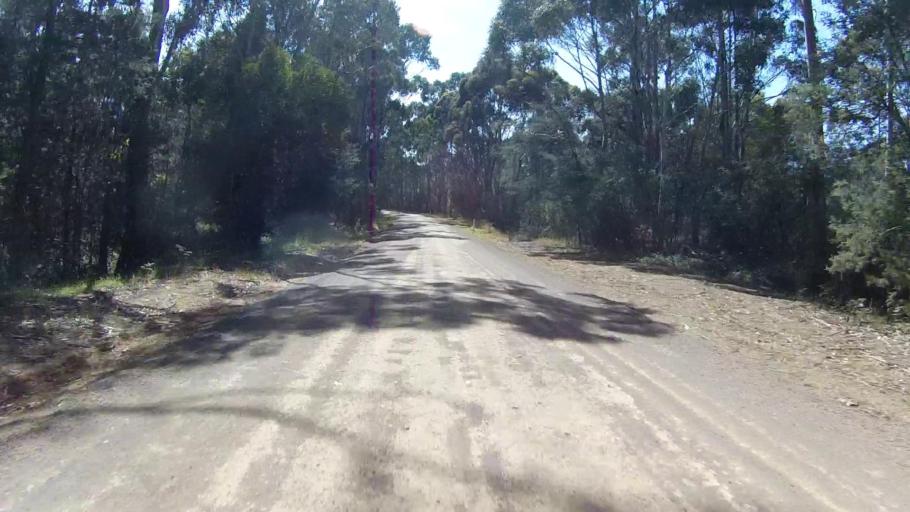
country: AU
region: Tasmania
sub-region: Sorell
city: Sorell
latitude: -42.7526
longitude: 147.6958
